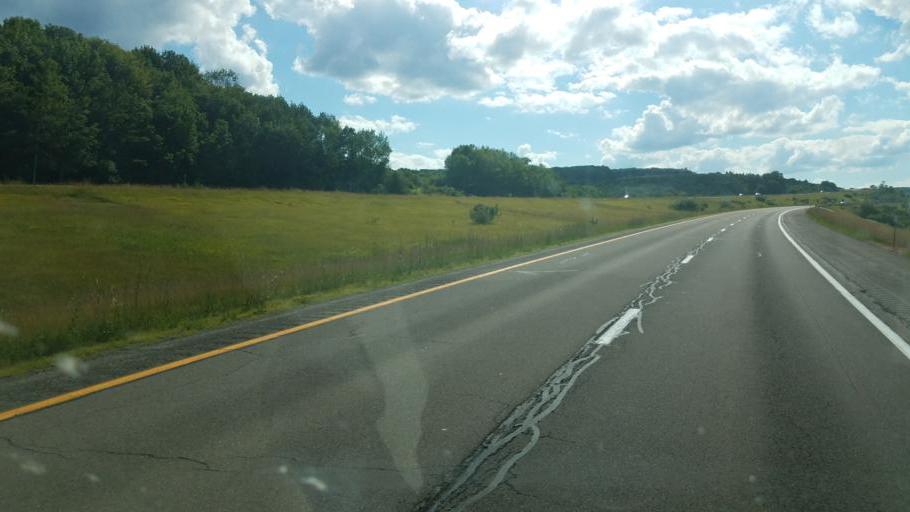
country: US
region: New York
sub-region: Allegany County
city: Alfred
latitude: 42.3181
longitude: -77.8176
